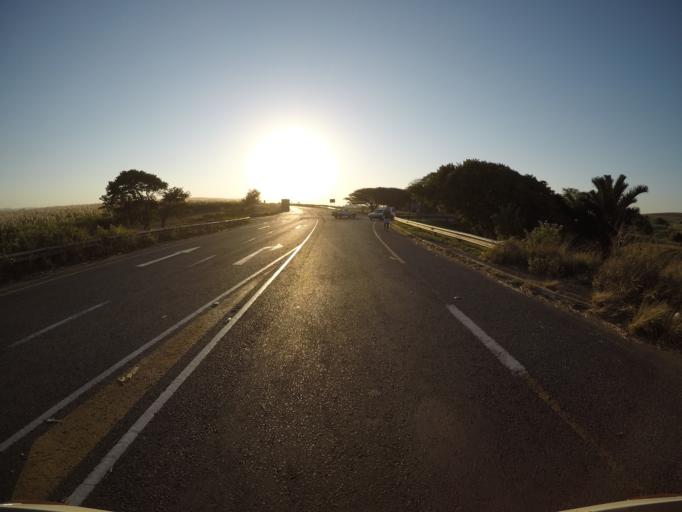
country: ZA
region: KwaZulu-Natal
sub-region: uThungulu District Municipality
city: eSikhawini
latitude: -28.9476
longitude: 31.7329
